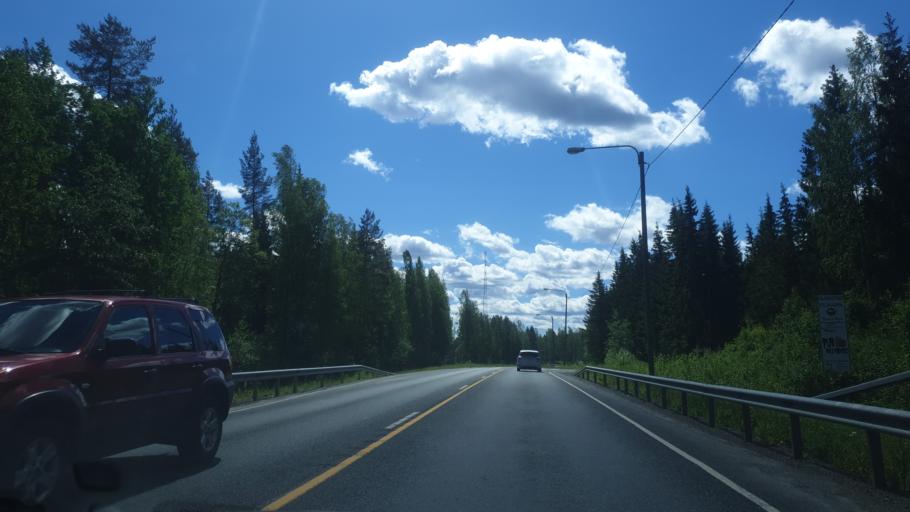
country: FI
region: Northern Savo
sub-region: Varkaus
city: Leppaevirta
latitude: 62.5862
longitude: 27.6052
